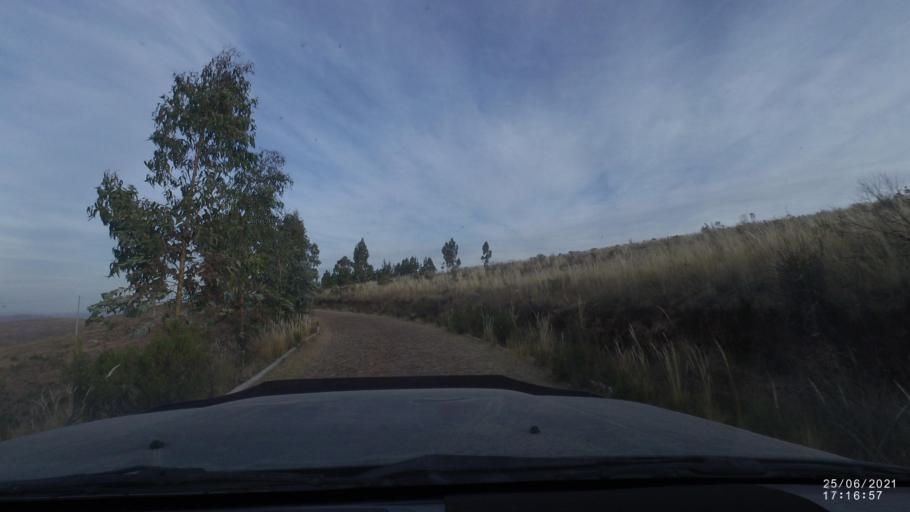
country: BO
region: Cochabamba
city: Arani
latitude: -17.8846
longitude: -65.7010
